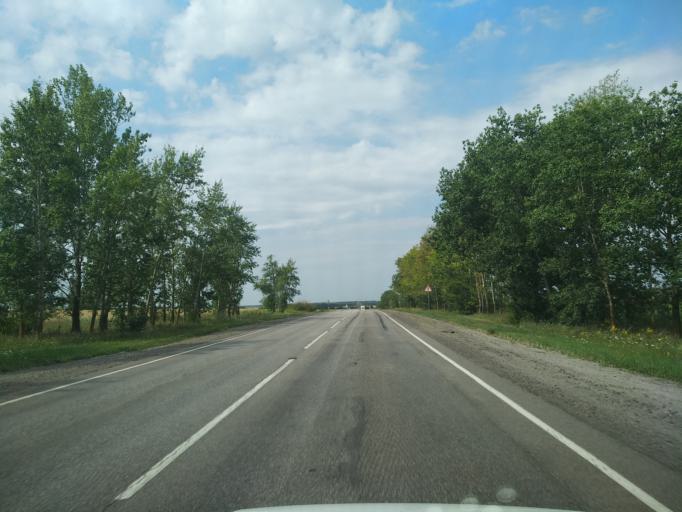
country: RU
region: Voronezj
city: Verkhnyaya Khava
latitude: 51.6943
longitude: 39.9491
